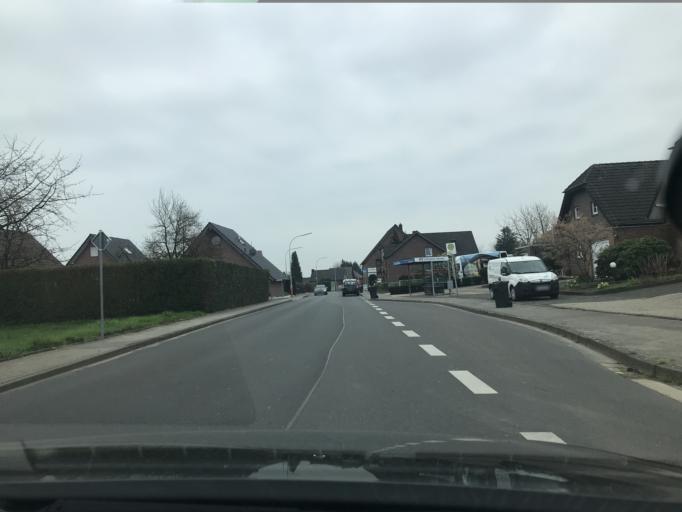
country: DE
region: North Rhine-Westphalia
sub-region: Regierungsbezirk Dusseldorf
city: Schwalmtal
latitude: 51.2240
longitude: 6.2435
